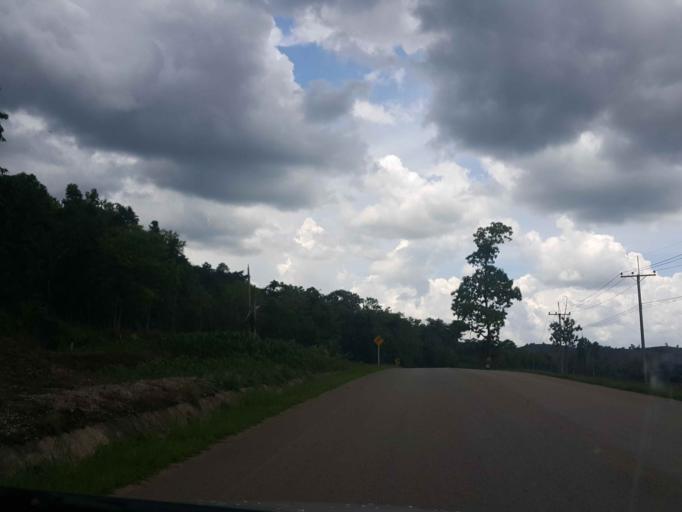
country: TH
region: Phayao
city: Dok Kham Tai
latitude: 18.9735
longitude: 100.0734
